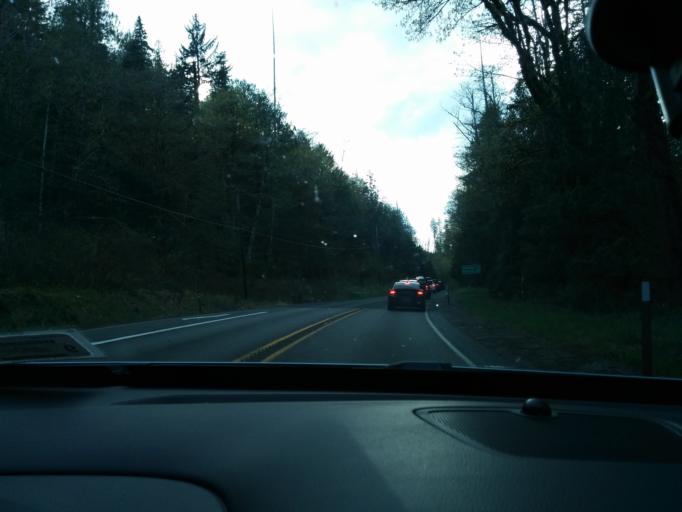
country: US
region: Washington
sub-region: Snohomish County
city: Gold Bar
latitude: 47.8125
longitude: -121.5800
